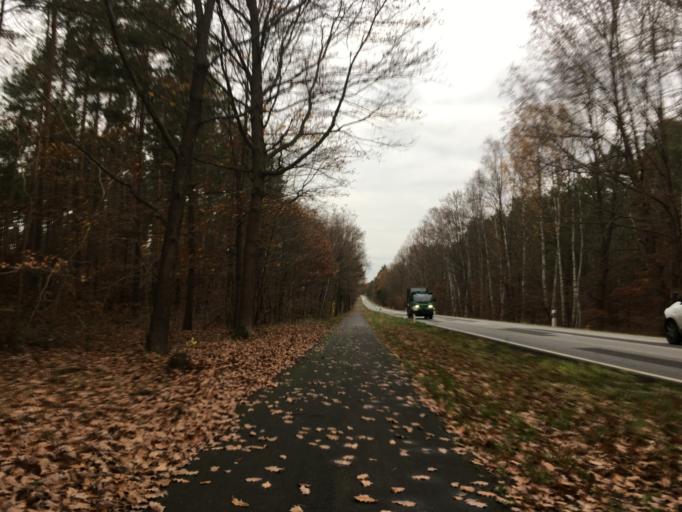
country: DE
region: Brandenburg
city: Mullrose
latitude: 52.2068
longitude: 14.4543
